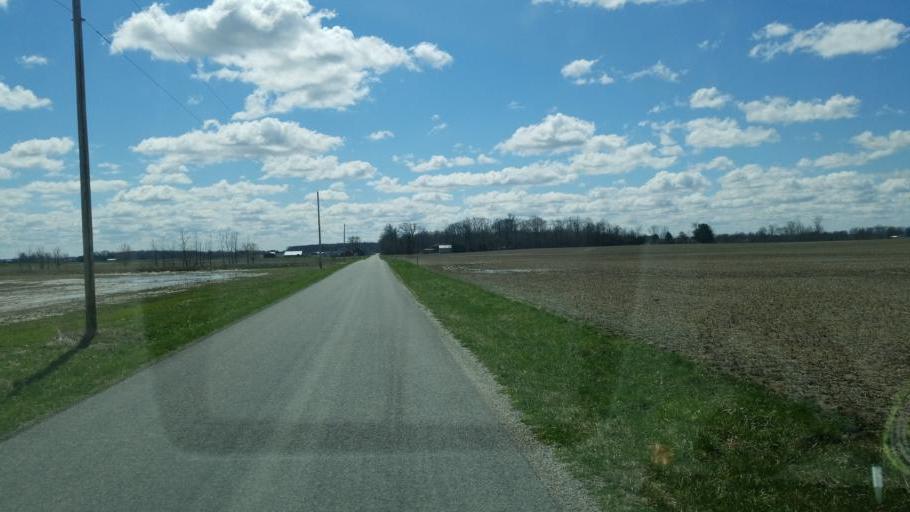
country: US
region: Ohio
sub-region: Hancock County
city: Findlay
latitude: 41.0511
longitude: -83.5150
